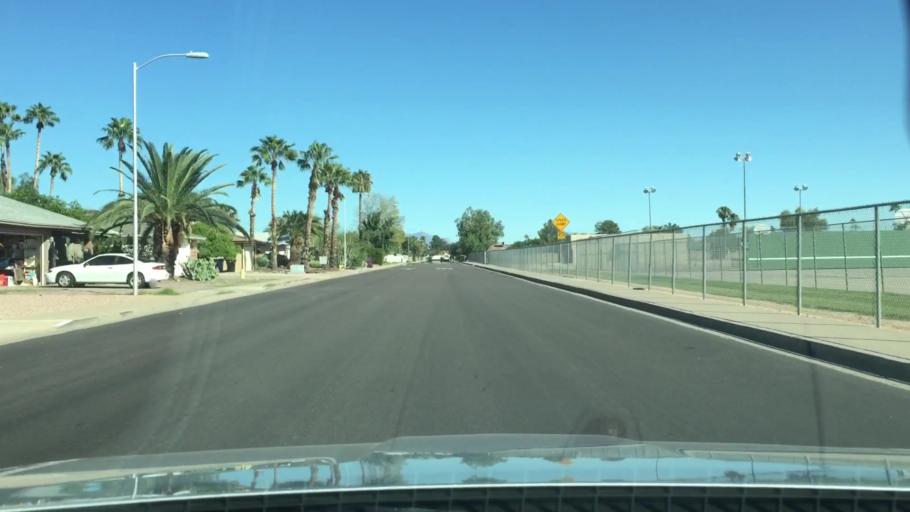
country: US
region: Arizona
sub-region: Maricopa County
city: Gilbert
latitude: 33.4046
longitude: -111.7604
